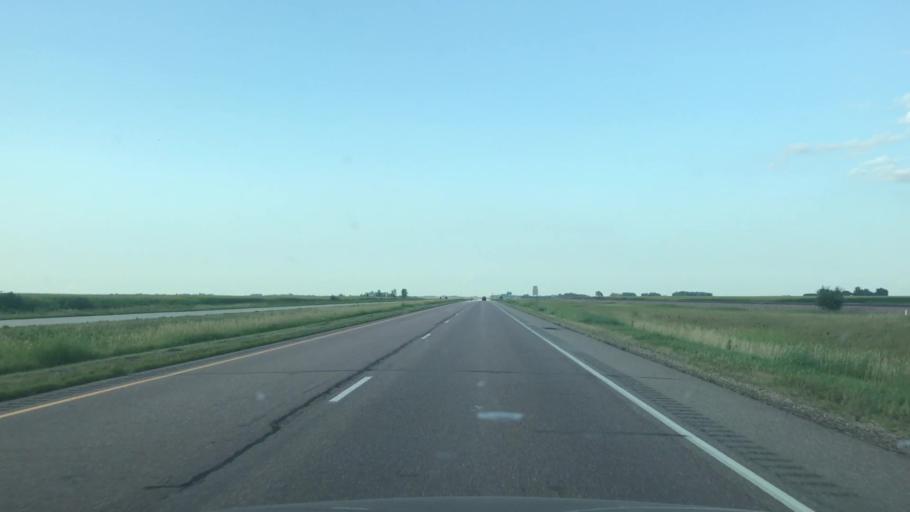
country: US
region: Minnesota
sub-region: Nobles County
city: Worthington
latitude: 43.7268
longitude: -95.4281
